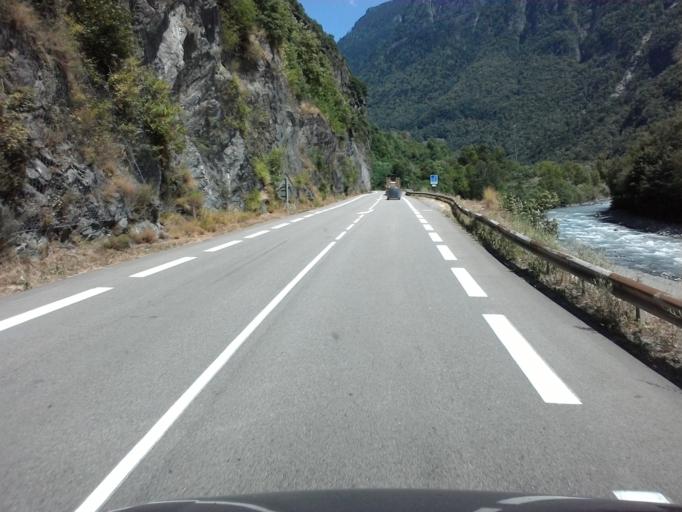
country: FR
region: Rhone-Alpes
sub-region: Departement de l'Isere
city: Vaulnaveys-le-Bas
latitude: 45.0526
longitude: 5.8413
